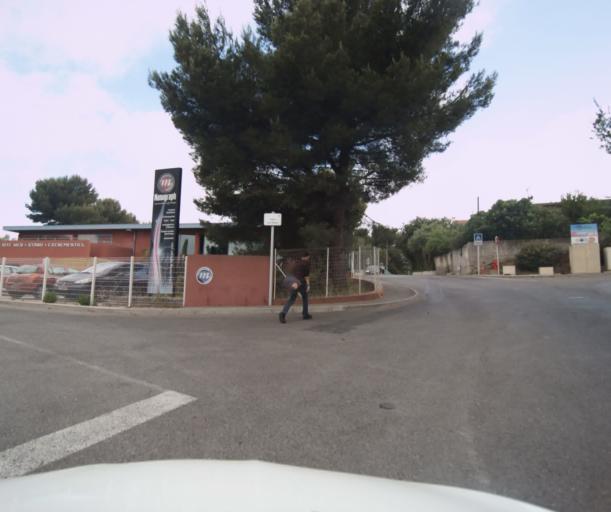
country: FR
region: Provence-Alpes-Cote d'Azur
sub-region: Departement du Var
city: Six-Fours-les-Plages
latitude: 43.1098
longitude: 5.8510
